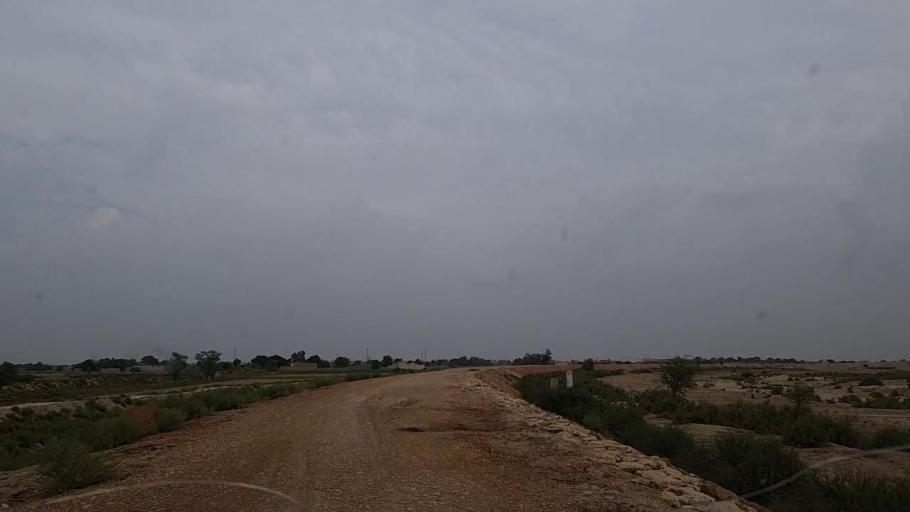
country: PK
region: Sindh
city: Johi
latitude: 26.7032
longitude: 67.5963
